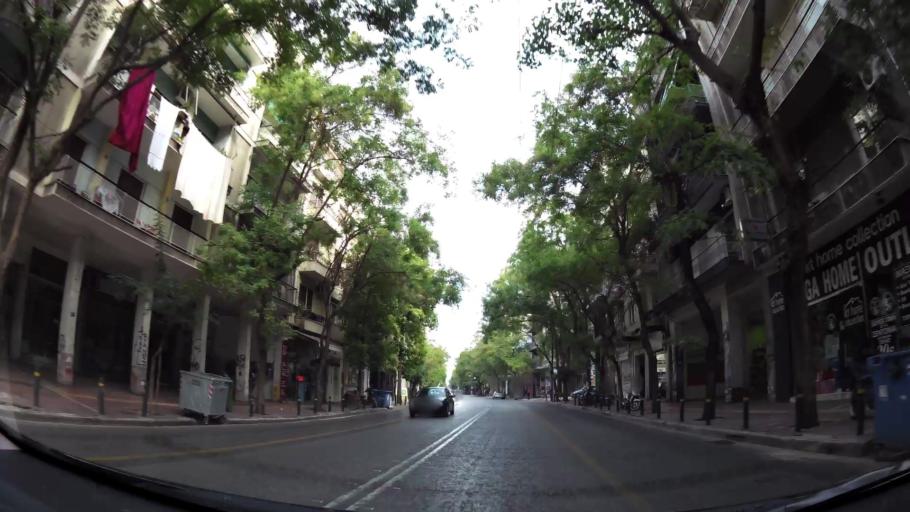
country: GR
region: Attica
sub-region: Nomarchia Athinas
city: Kipseli
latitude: 38.0062
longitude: 23.7350
